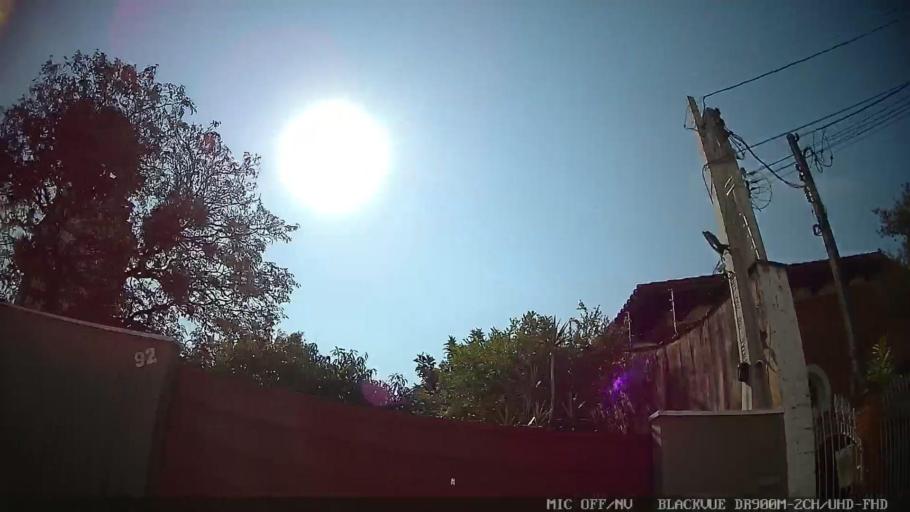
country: BR
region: Sao Paulo
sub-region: Itatiba
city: Itatiba
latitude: -23.0082
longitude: -46.8371
